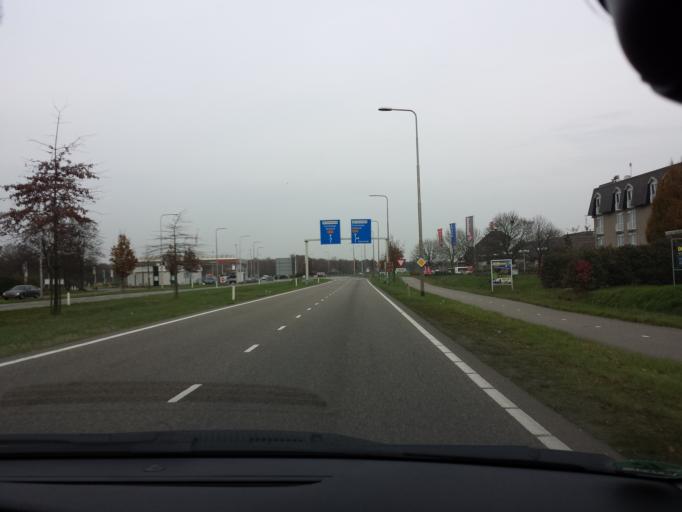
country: NL
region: Limburg
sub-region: Gemeente Peel en Maas
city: Maasbree
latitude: 51.3781
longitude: 5.9845
